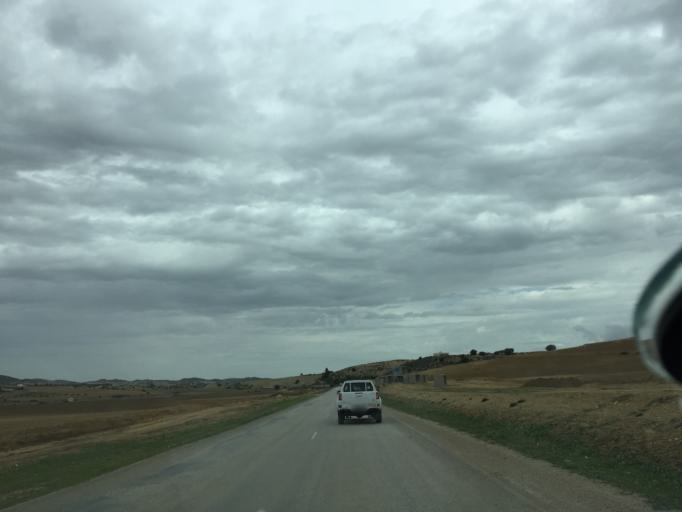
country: TN
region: Silyanah
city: Bu `Aradah
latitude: 36.2083
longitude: 9.7301
